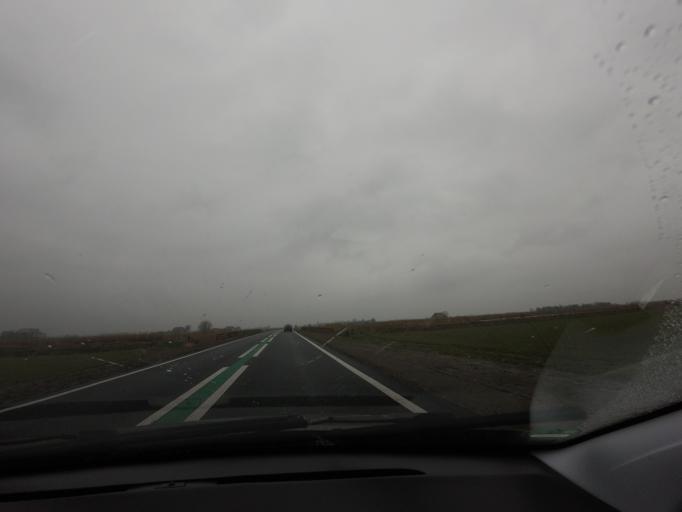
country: NL
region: Friesland
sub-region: Sudwest Fryslan
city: Workum
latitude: 53.0009
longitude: 5.4683
